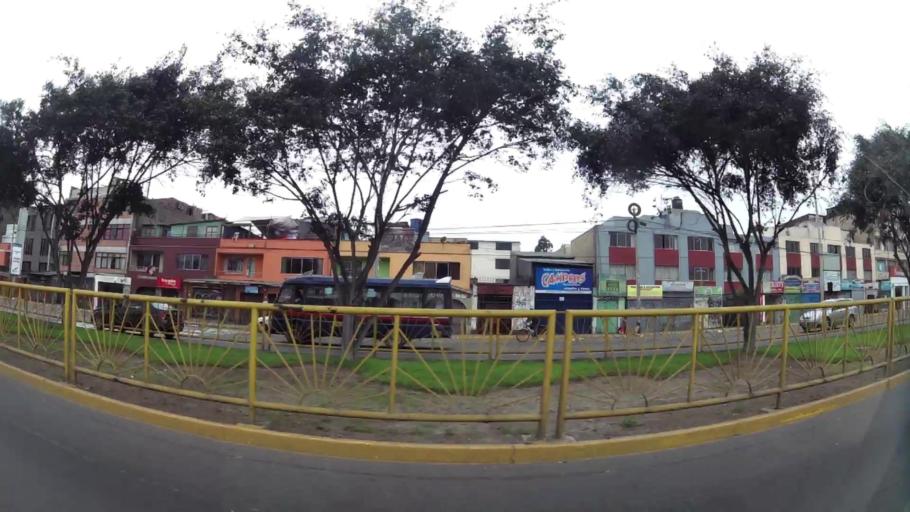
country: PE
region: Lima
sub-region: Lima
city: San Luis
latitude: -12.0843
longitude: -77.0050
